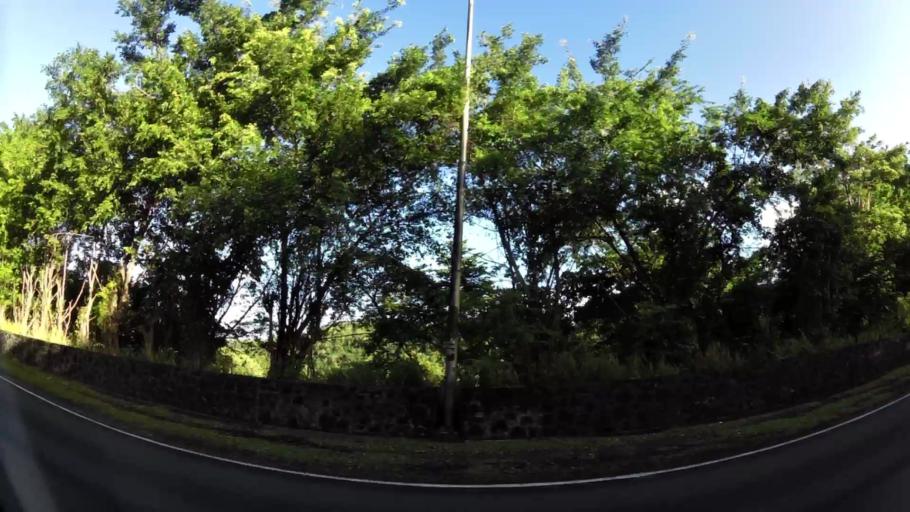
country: LC
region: Castries Quarter
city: Castries
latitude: 14.0042
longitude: -61.0038
